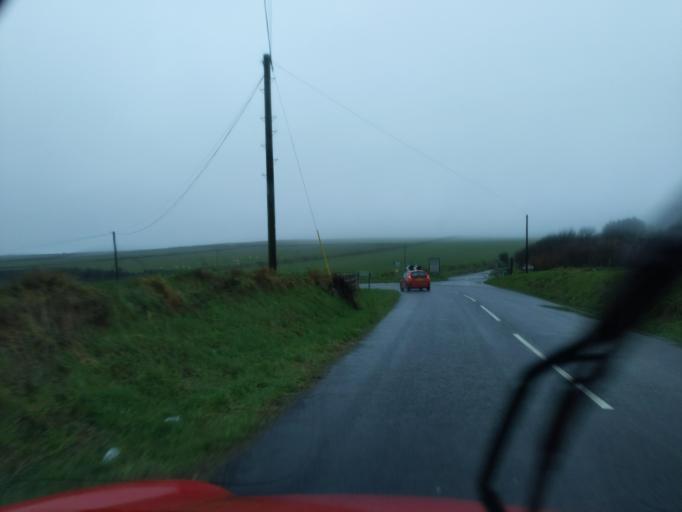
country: GB
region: England
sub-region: Cornwall
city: Camelford
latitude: 50.6457
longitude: -4.6982
